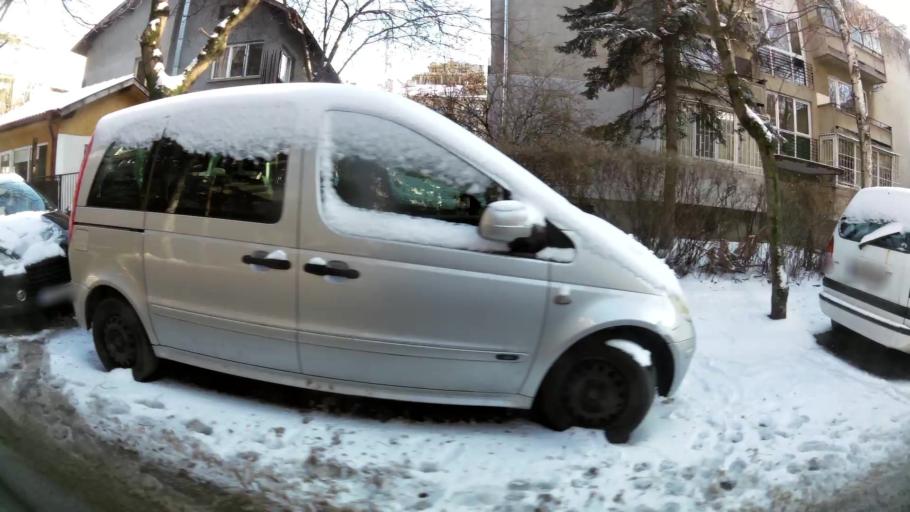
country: BG
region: Sofia-Capital
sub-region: Stolichna Obshtina
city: Sofia
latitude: 42.6697
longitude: 23.3621
